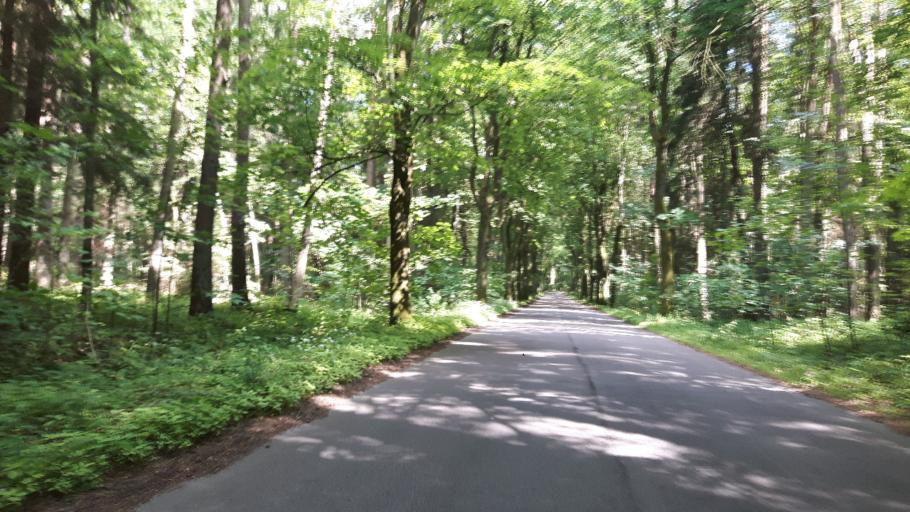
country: PL
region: West Pomeranian Voivodeship
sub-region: Powiat goleniowski
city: Nowogard
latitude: 53.6715
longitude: 15.0843
